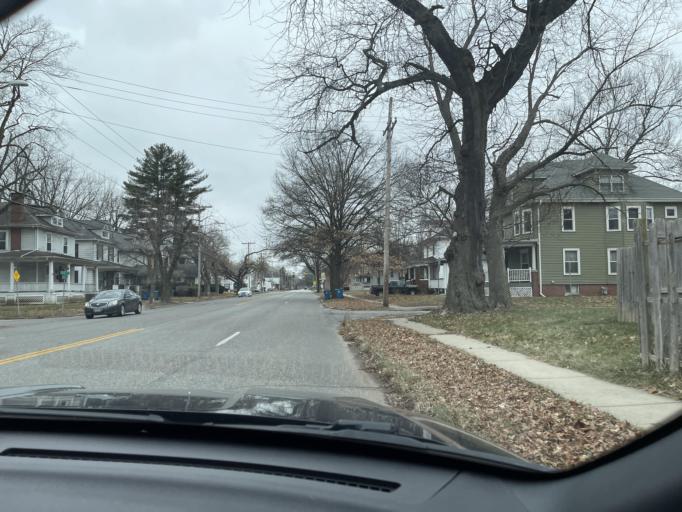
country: US
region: Illinois
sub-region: Sangamon County
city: Leland Grove
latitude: 39.7943
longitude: -89.6661
